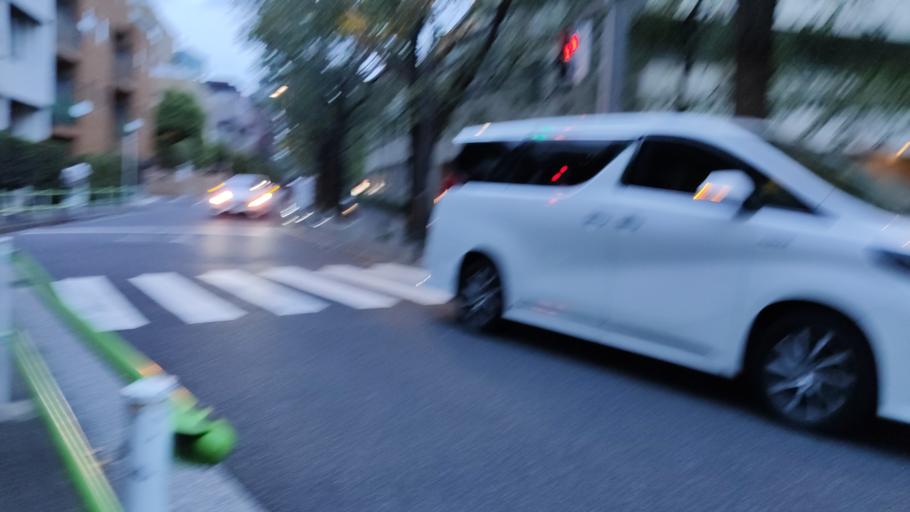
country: JP
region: Tokyo
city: Tokyo
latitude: 35.6537
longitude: 139.7311
